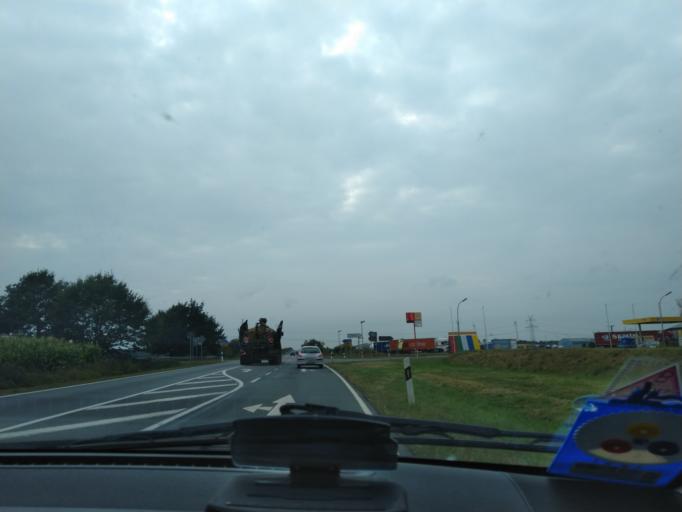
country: DE
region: Lower Saxony
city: Rhede
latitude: 53.0641
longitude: 7.2486
